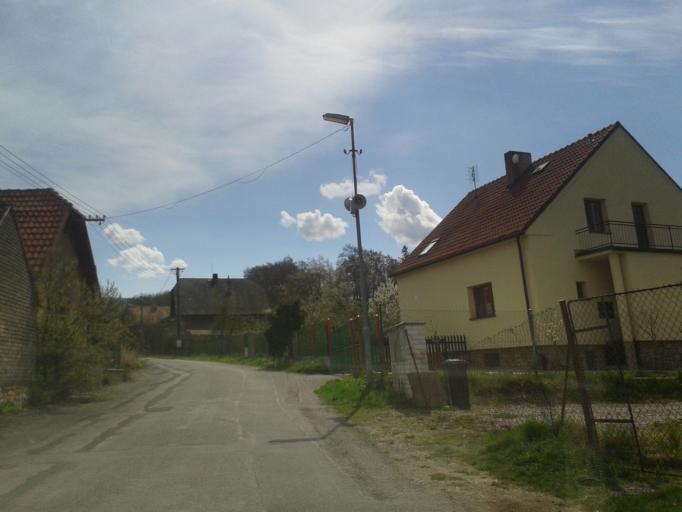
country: CZ
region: Central Bohemia
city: Dobris
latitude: 49.8687
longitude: 14.1418
